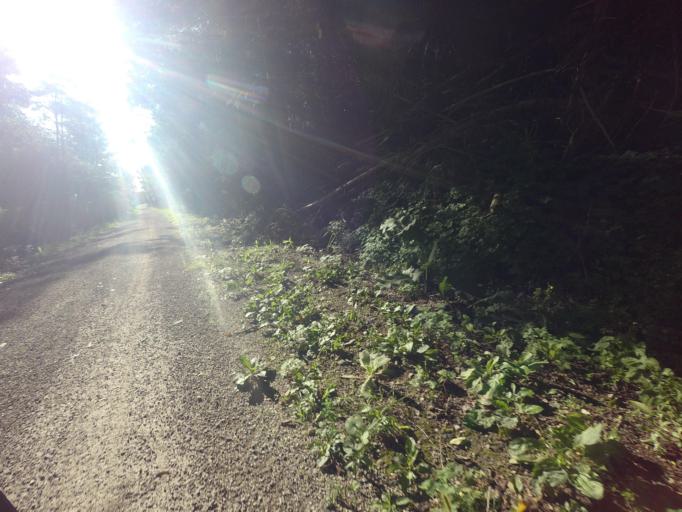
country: CA
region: Ontario
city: Goderich
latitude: 43.7436
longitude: -81.4891
